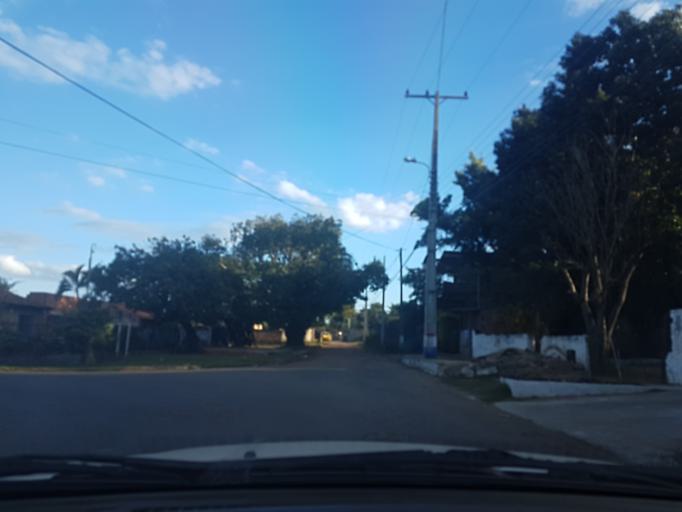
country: PY
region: Central
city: Colonia Mariano Roque Alonso
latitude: -25.2368
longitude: -57.5294
